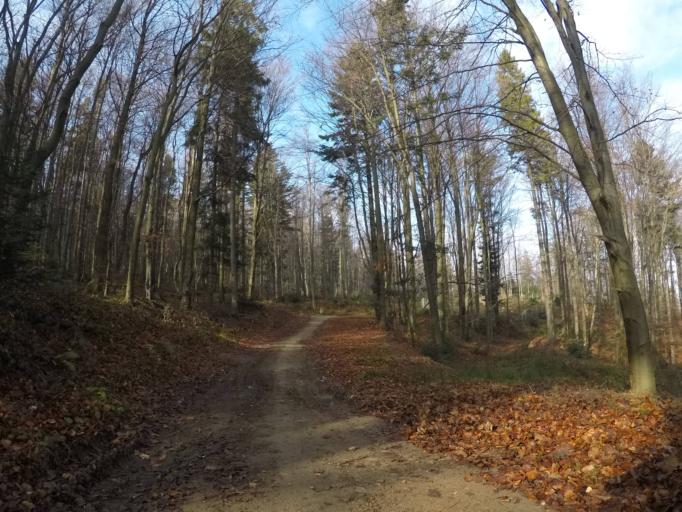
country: SK
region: Kosicky
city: Moldava nad Bodvou
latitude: 48.7637
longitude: 21.0847
